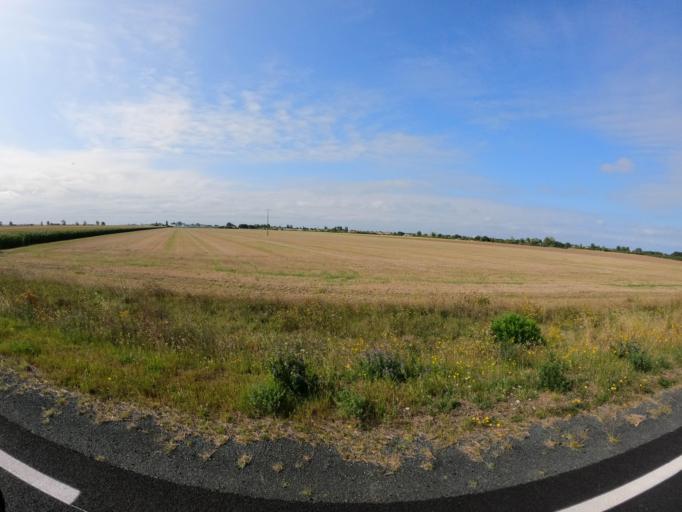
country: FR
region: Pays de la Loire
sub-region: Departement de la Vendee
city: Triaize
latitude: 46.3410
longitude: -1.2933
